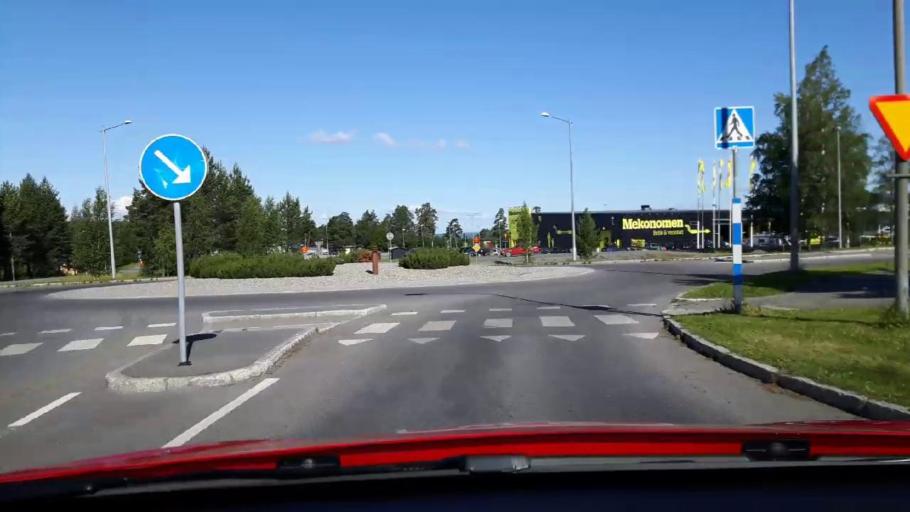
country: SE
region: Jaemtland
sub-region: OEstersunds Kommun
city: Ostersund
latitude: 63.1881
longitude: 14.6529
